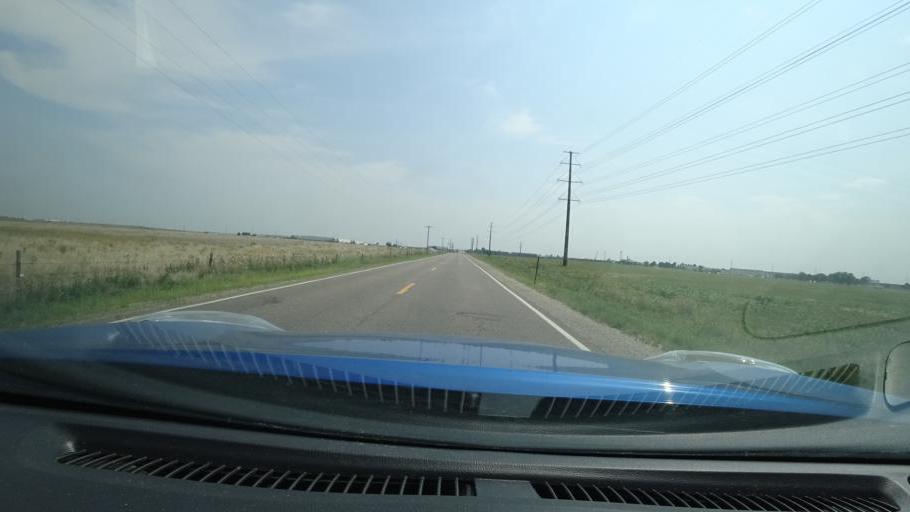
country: US
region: Colorado
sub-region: Adams County
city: Aurora
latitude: 39.7625
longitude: -104.7346
